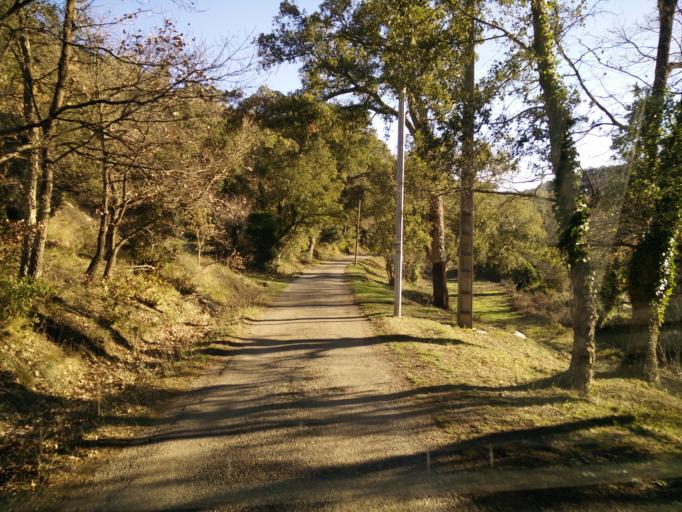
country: FR
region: Provence-Alpes-Cote d'Azur
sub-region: Departement du Var
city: Collobrieres
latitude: 43.2522
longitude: 6.3097
